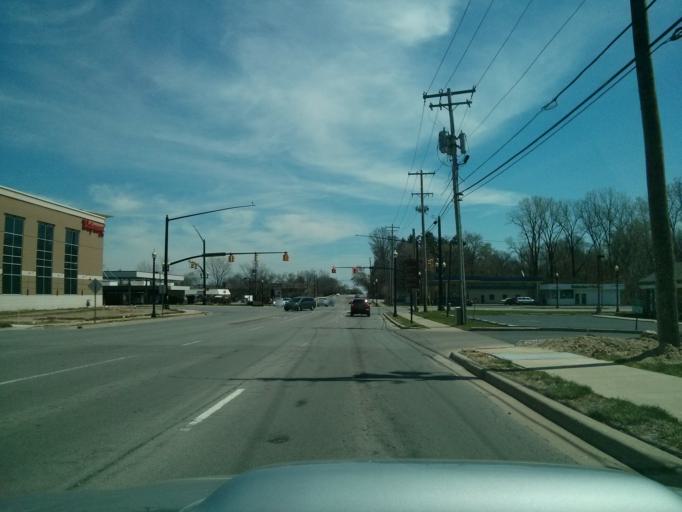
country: US
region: Indiana
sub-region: Hamilton County
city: Carmel
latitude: 39.9565
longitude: -86.1277
